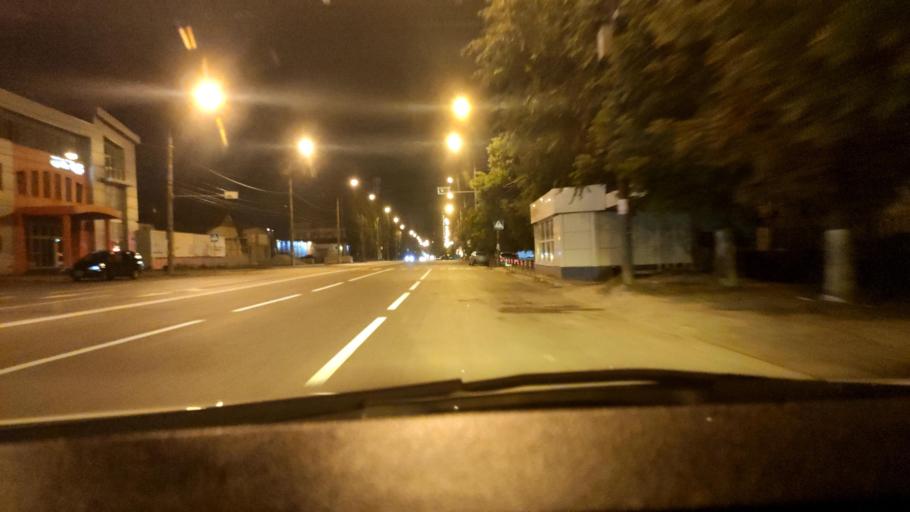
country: RU
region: Voronezj
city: Voronezh
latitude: 51.6869
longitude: 39.1640
